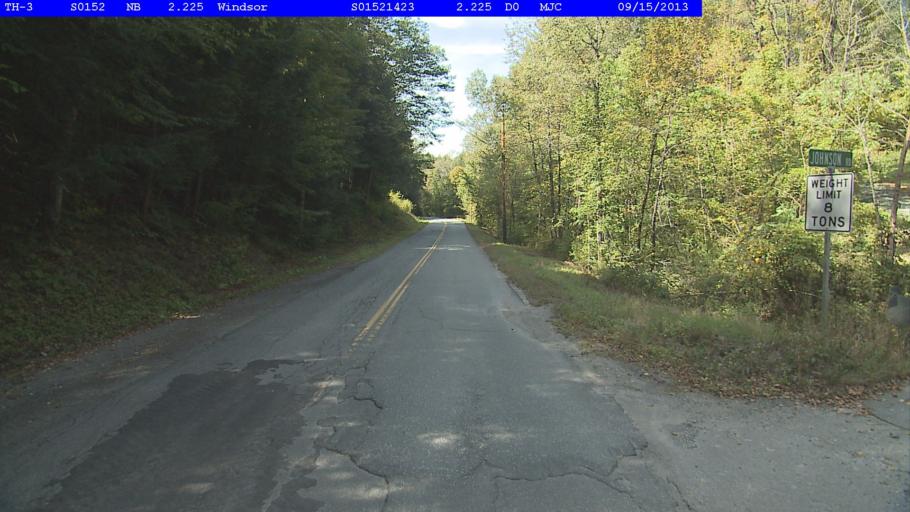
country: US
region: Vermont
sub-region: Windsor County
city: Windsor
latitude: 43.5008
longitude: -72.4150
